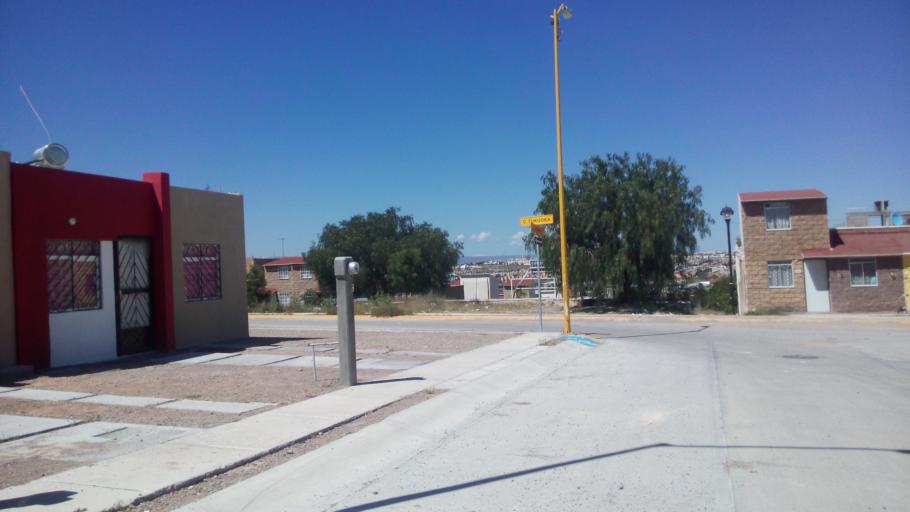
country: MX
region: Aguascalientes
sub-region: Aguascalientes
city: Cumbres III
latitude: 21.8738
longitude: -102.2289
